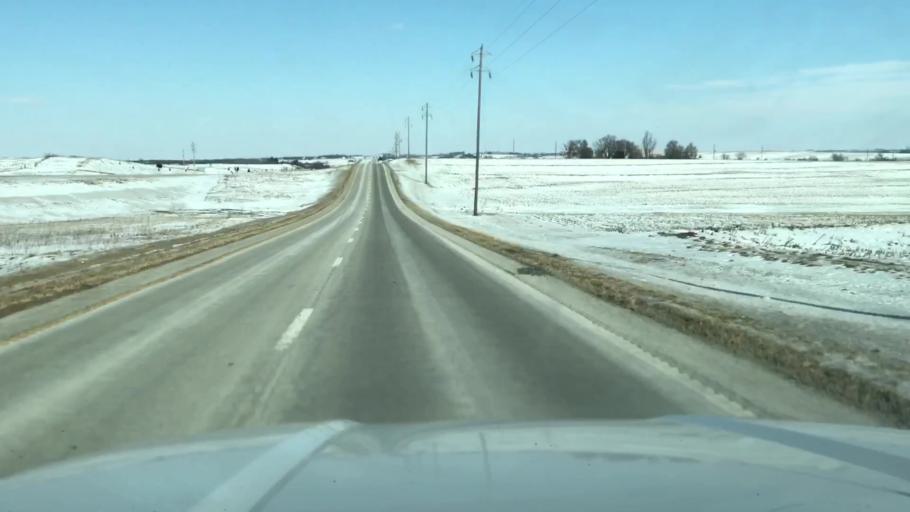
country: US
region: Missouri
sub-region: Andrew County
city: Savannah
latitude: 40.1238
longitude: -94.8696
